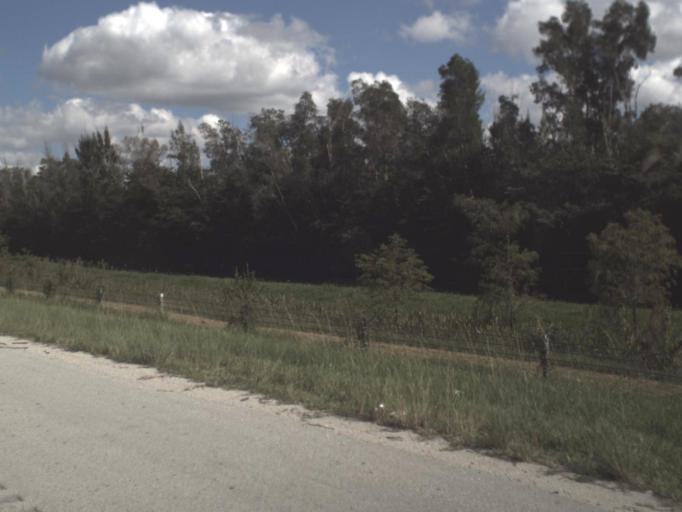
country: US
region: Florida
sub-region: Miami-Dade County
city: Palm Springs North
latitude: 25.9159
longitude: -80.3797
